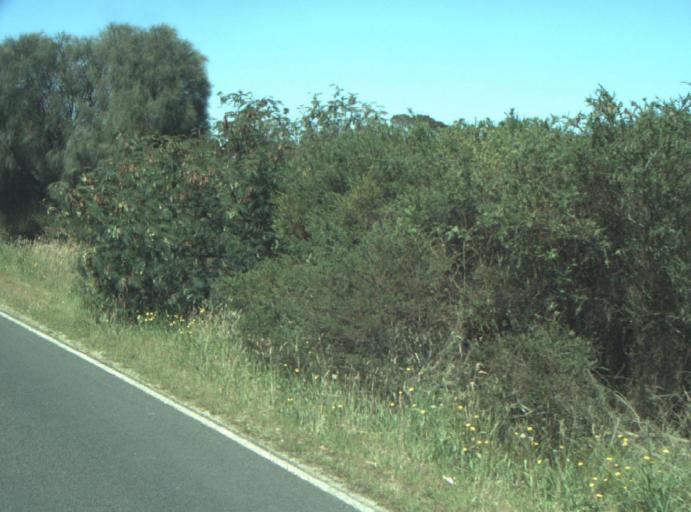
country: AU
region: Victoria
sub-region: Greater Geelong
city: Breakwater
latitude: -38.2314
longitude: 144.3545
